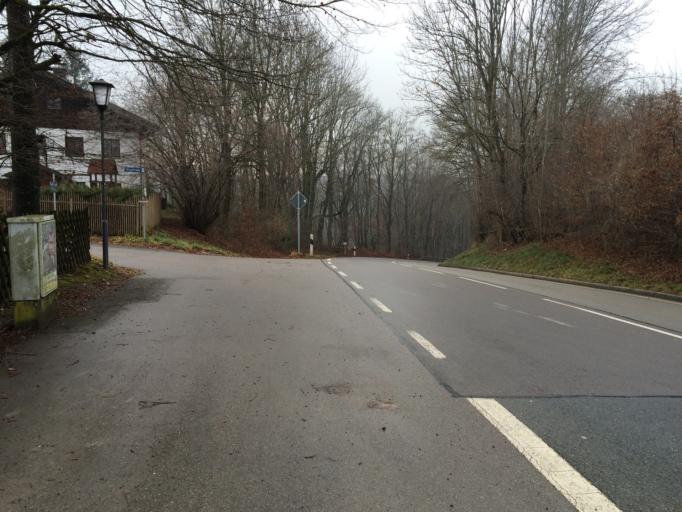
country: DE
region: Bavaria
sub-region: Upper Bavaria
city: Weyarn
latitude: 47.8618
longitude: 11.7936
